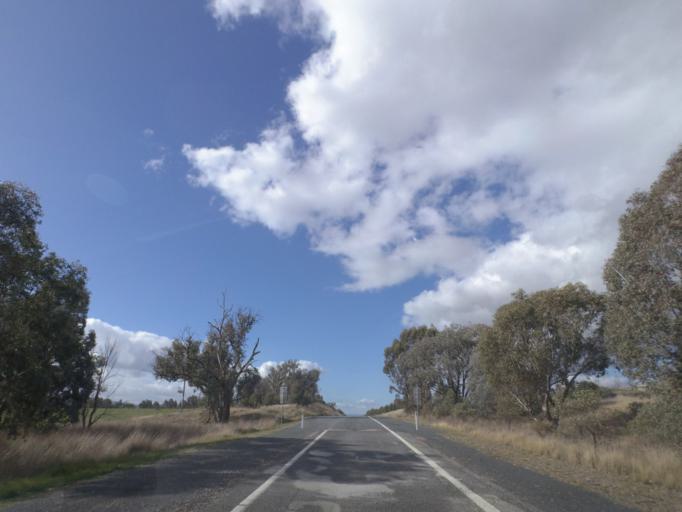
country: AU
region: New South Wales
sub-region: Greater Hume Shire
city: Holbrook
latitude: -35.6839
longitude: 147.3588
